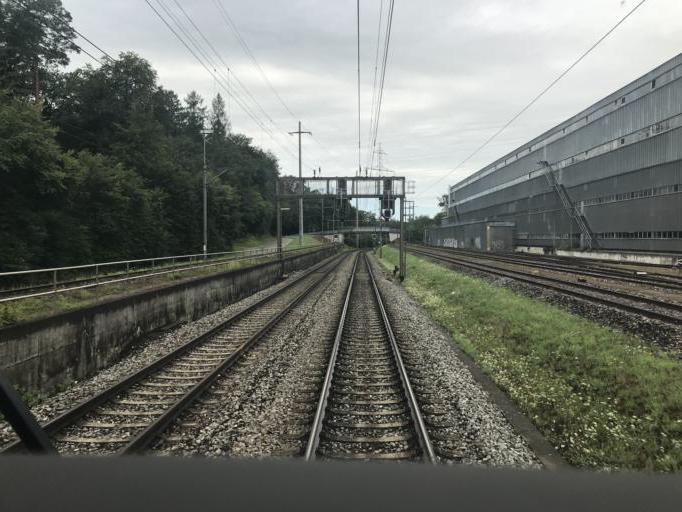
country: CH
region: Zurich
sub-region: Bezirk Buelach
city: Hochfelden
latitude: 47.5305
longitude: 8.5272
